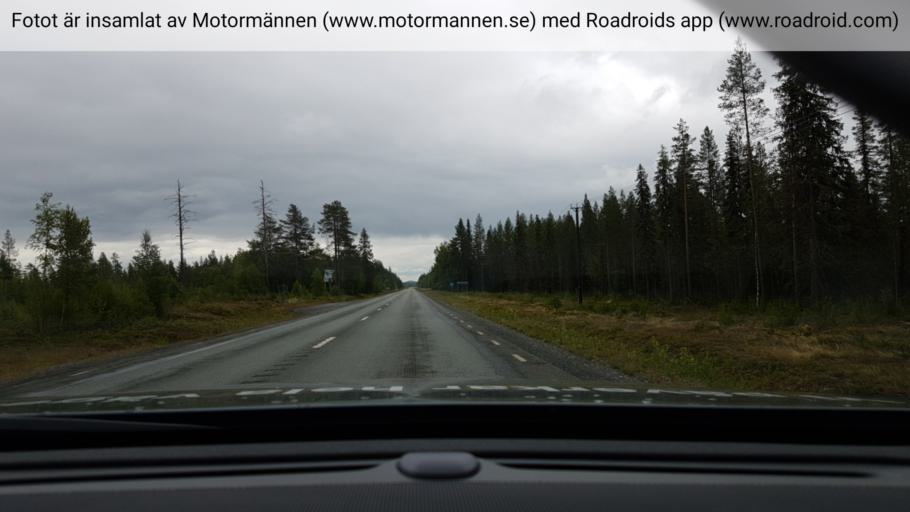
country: SE
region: Vaesterbotten
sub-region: Norsjo Kommun
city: Norsjoe
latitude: 65.2397
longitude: 19.7163
